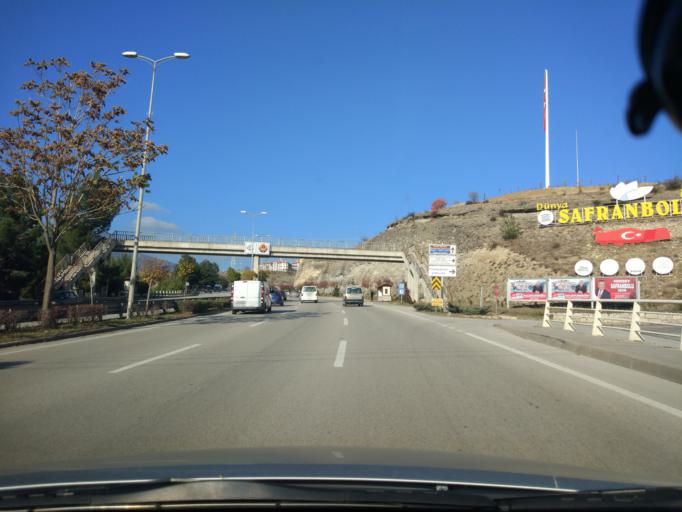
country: TR
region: Karabuk
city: Safranbolu
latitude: 41.2323
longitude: 32.6724
